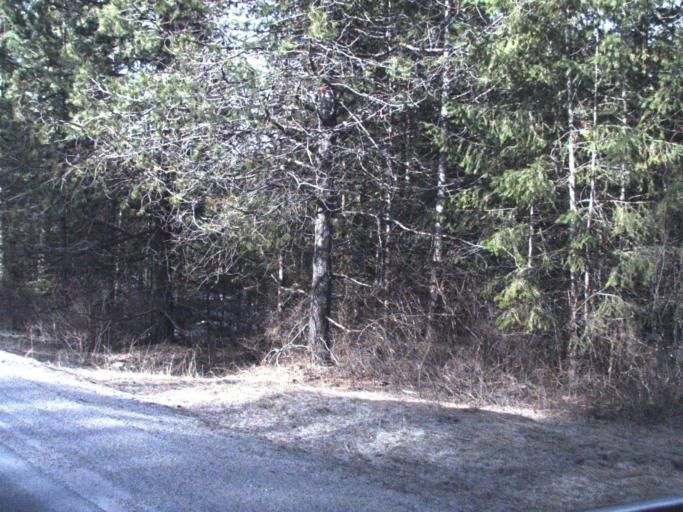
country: US
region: Washington
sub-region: Stevens County
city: Colville
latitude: 48.5147
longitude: -117.6985
